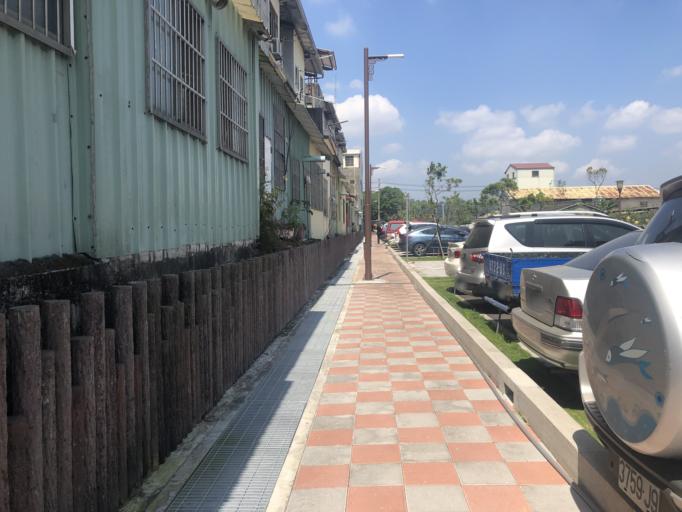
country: TW
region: Taiwan
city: Fengyuan
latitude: 24.2037
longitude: 120.8409
